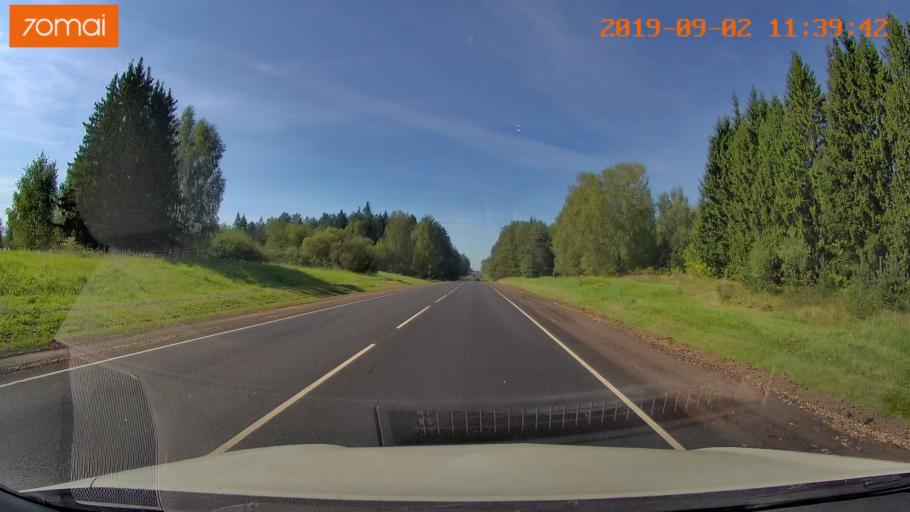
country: RU
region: Smolensk
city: Oster
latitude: 53.9064
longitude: 32.7178
